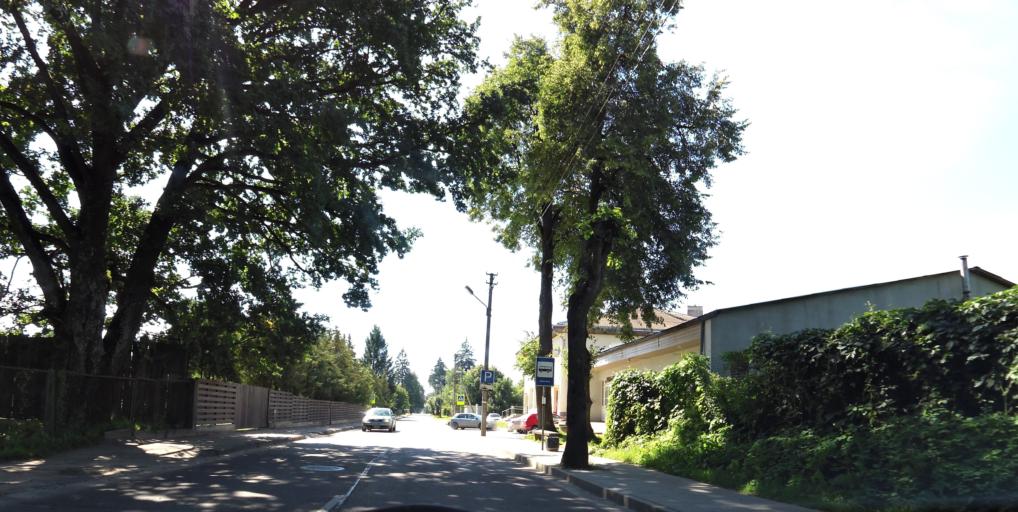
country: LT
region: Vilnius County
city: Rasos
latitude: 54.6713
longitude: 25.3612
